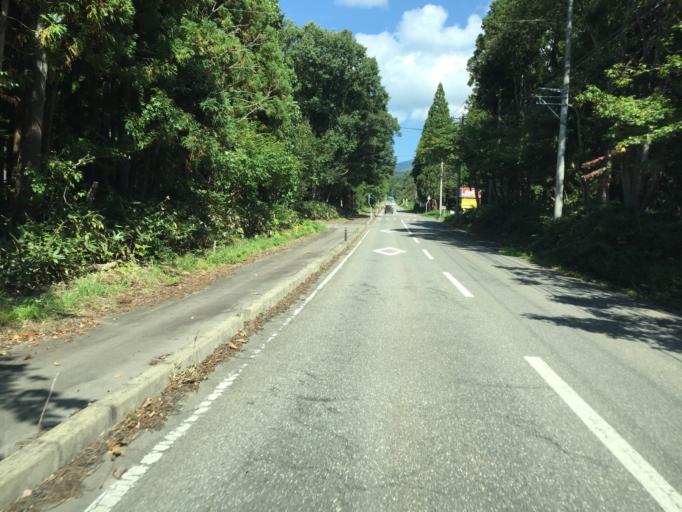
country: JP
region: Fukushima
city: Inawashiro
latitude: 37.5645
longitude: 140.0097
